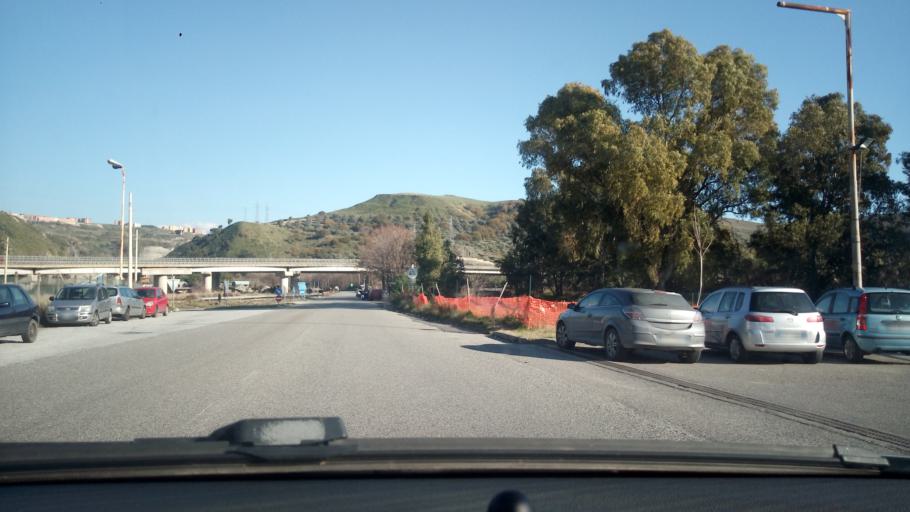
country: IT
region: Calabria
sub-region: Provincia di Catanzaro
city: Settingiano
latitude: 38.8928
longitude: 16.5516
